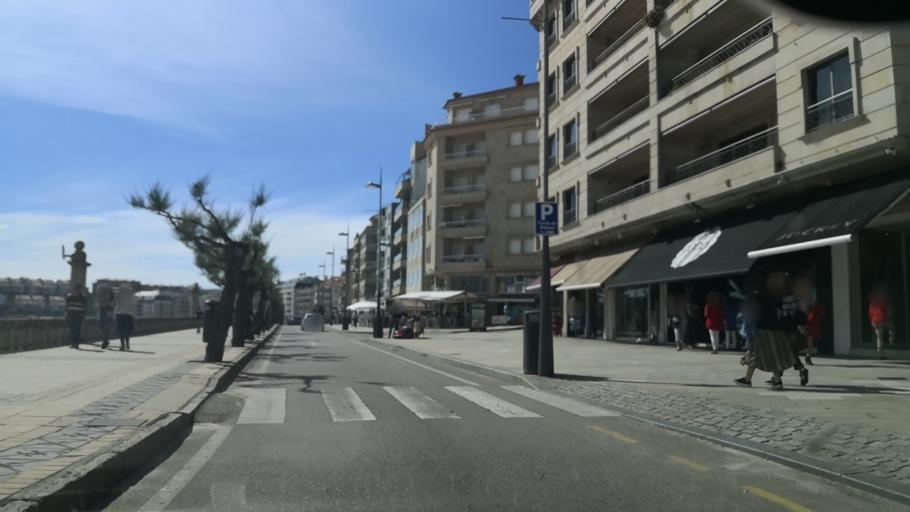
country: ES
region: Galicia
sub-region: Provincia de Pontevedra
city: Sanxenxo
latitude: 42.4011
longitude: -8.8093
